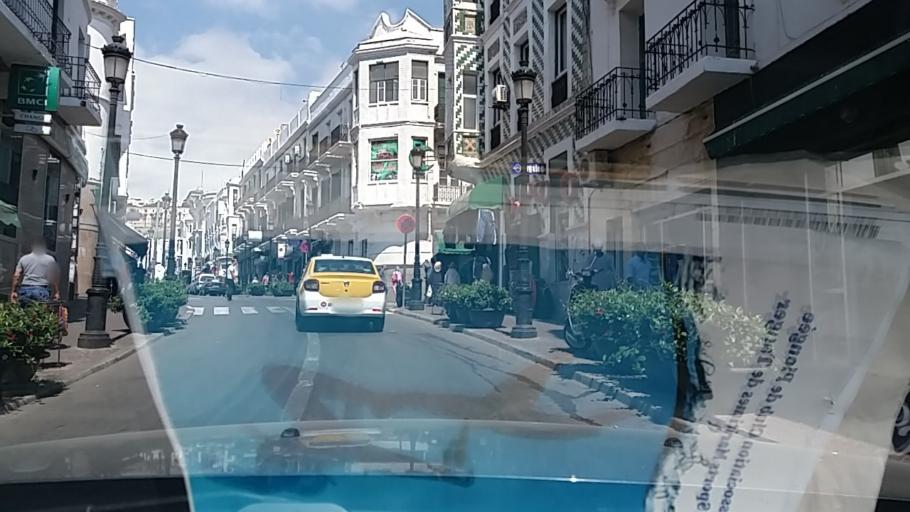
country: MA
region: Tanger-Tetouan
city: Tetouan
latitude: 35.5693
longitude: -5.3721
